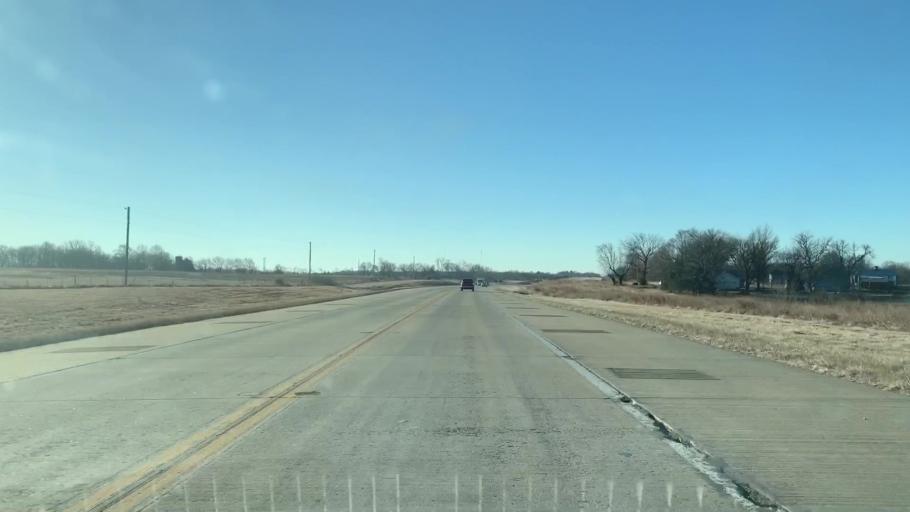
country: US
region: Kansas
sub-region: Crawford County
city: Arma
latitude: 37.5760
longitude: -94.7052
